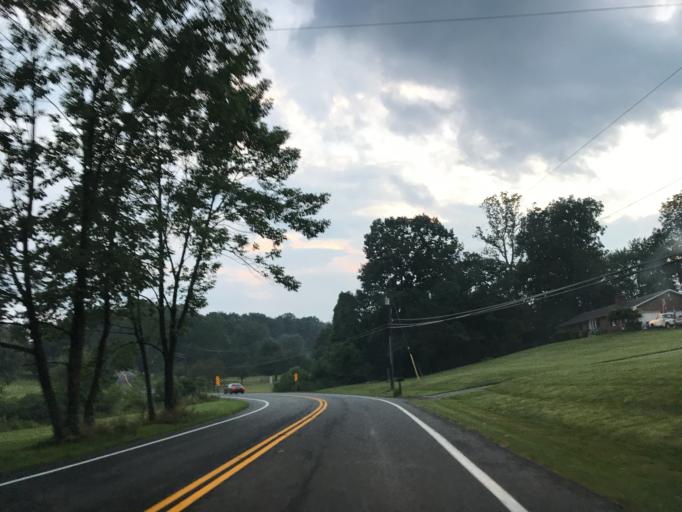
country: US
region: Maryland
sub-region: Harford County
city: Fallston
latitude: 39.5195
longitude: -76.4015
